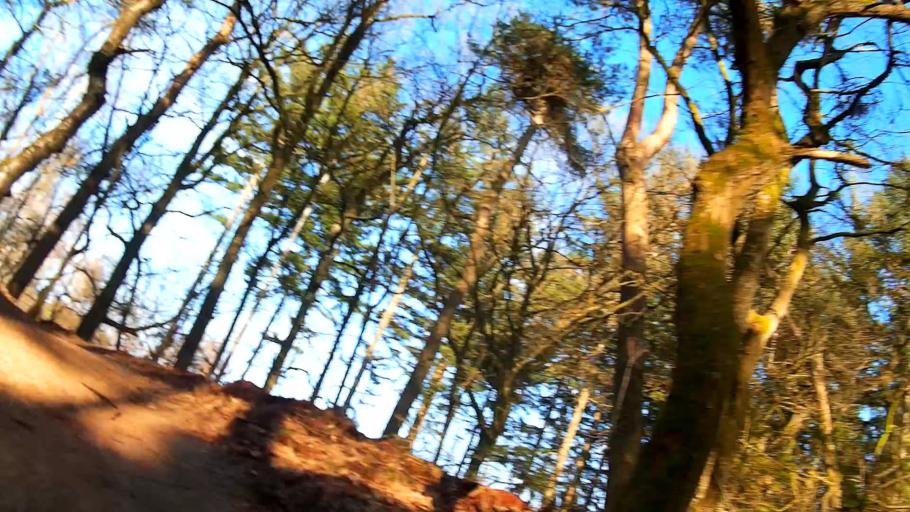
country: NL
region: Utrecht
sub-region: Gemeente Utrechtse Heuvelrug
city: Leersum
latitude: 52.0364
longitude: 5.4468
